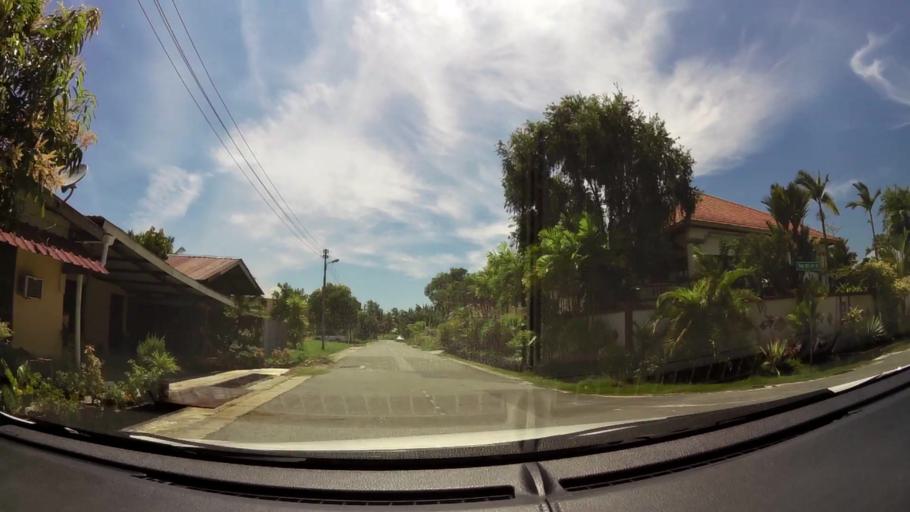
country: BN
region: Brunei and Muara
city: Bandar Seri Begawan
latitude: 4.9368
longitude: 114.9511
